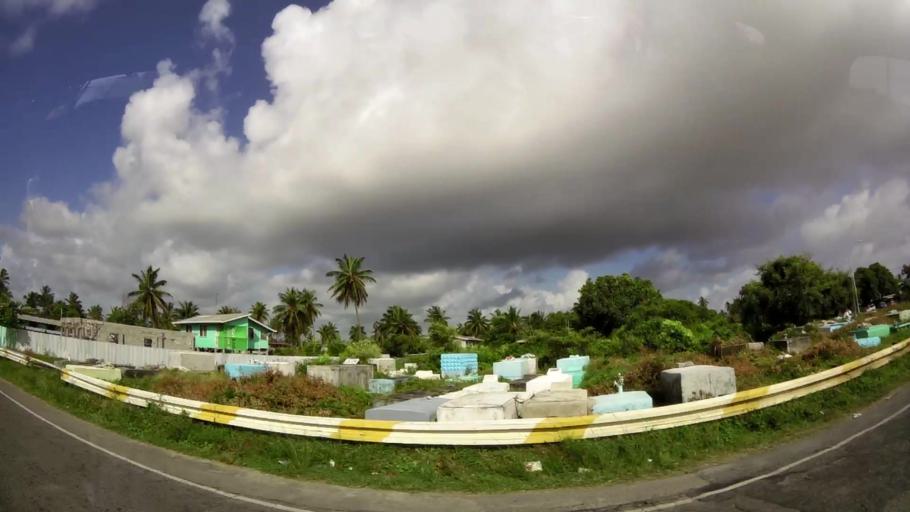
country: GY
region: Demerara-Mahaica
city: Mahaica Village
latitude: 6.7737
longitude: -57.9987
